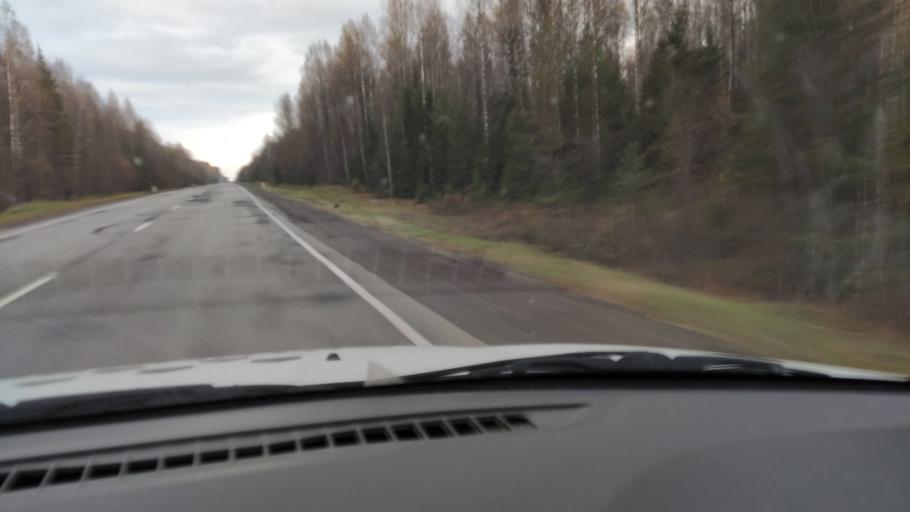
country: RU
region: Kirov
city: Omutninsk
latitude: 58.7671
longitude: 51.9747
